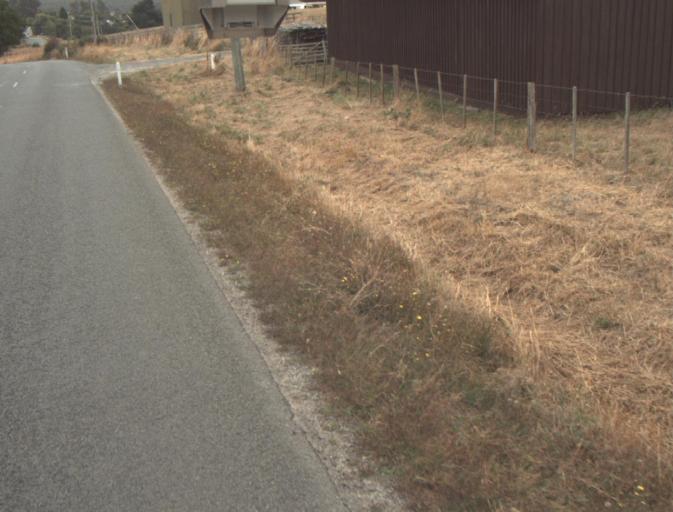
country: AU
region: Tasmania
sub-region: Launceston
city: Mayfield
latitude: -41.1948
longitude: 147.2208
